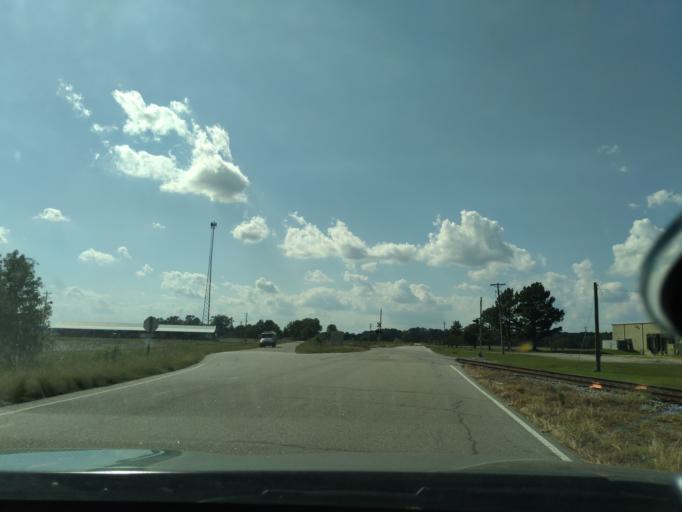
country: US
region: North Carolina
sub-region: Martin County
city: Robersonville
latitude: 35.8285
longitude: -77.2210
